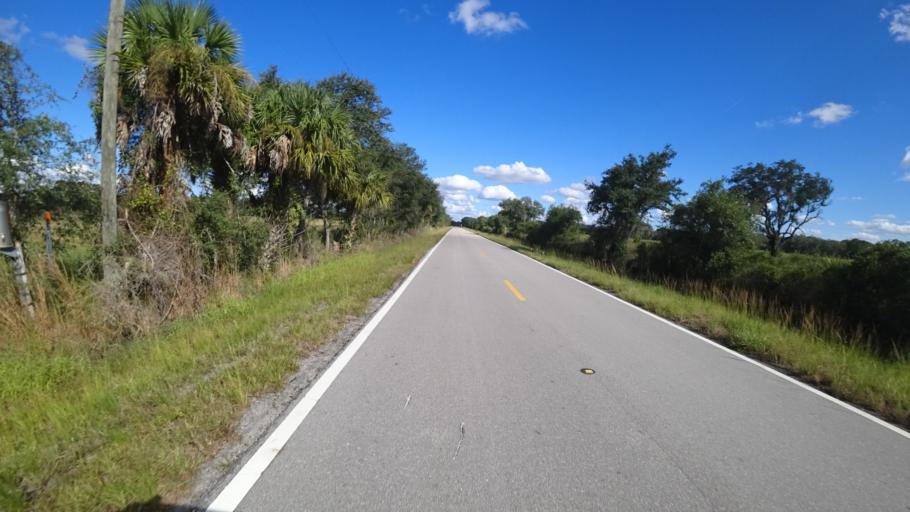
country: US
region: Florida
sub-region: Sarasota County
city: Lake Sarasota
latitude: 27.2904
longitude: -82.2395
